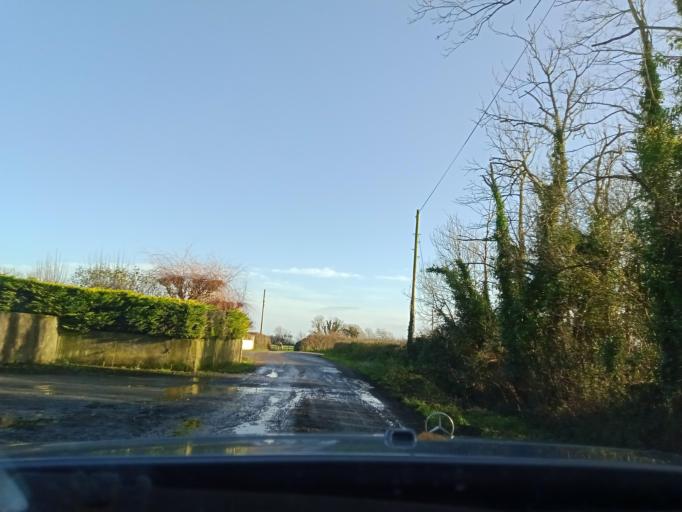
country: IE
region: Leinster
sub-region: Kilkenny
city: Callan
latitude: 52.4807
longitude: -7.3946
